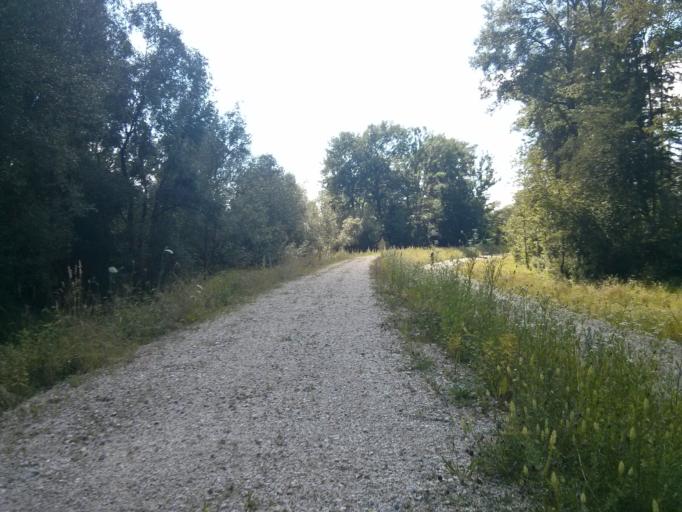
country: DE
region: Bavaria
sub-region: Lower Bavaria
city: Moos
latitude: 48.7864
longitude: 12.9408
